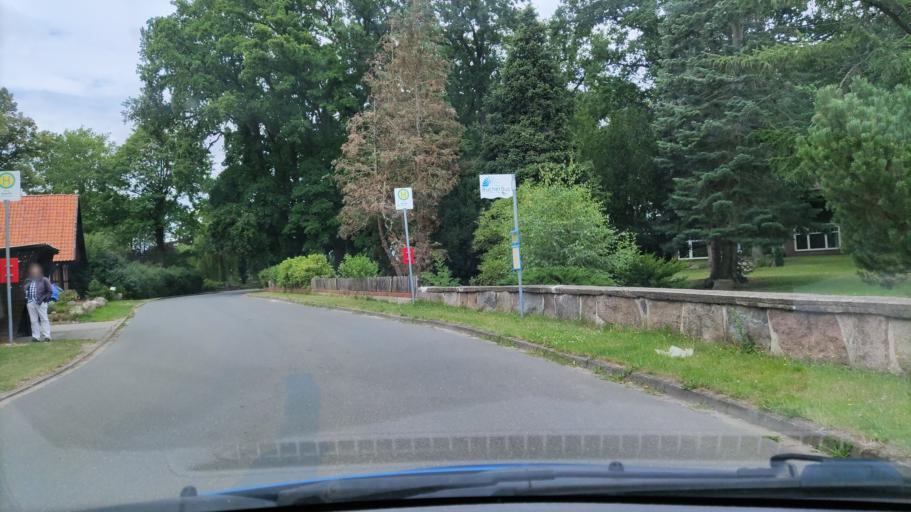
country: DE
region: Lower Saxony
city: Weste
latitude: 53.0596
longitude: 10.7033
